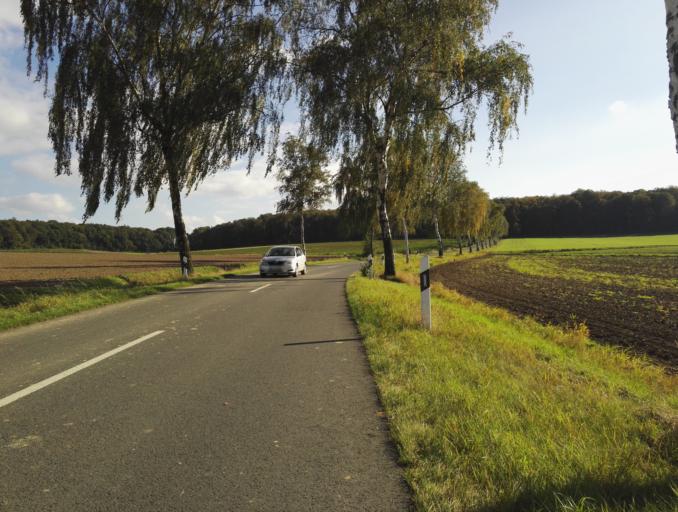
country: DE
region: Lower Saxony
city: Schellerten
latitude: 52.1412
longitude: 10.1354
